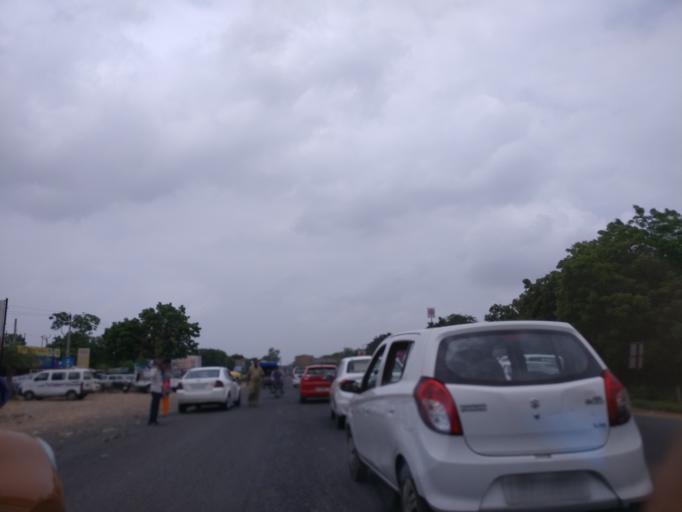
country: IN
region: Gujarat
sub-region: Gandhinagar
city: Adalaj
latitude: 23.1757
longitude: 72.5748
